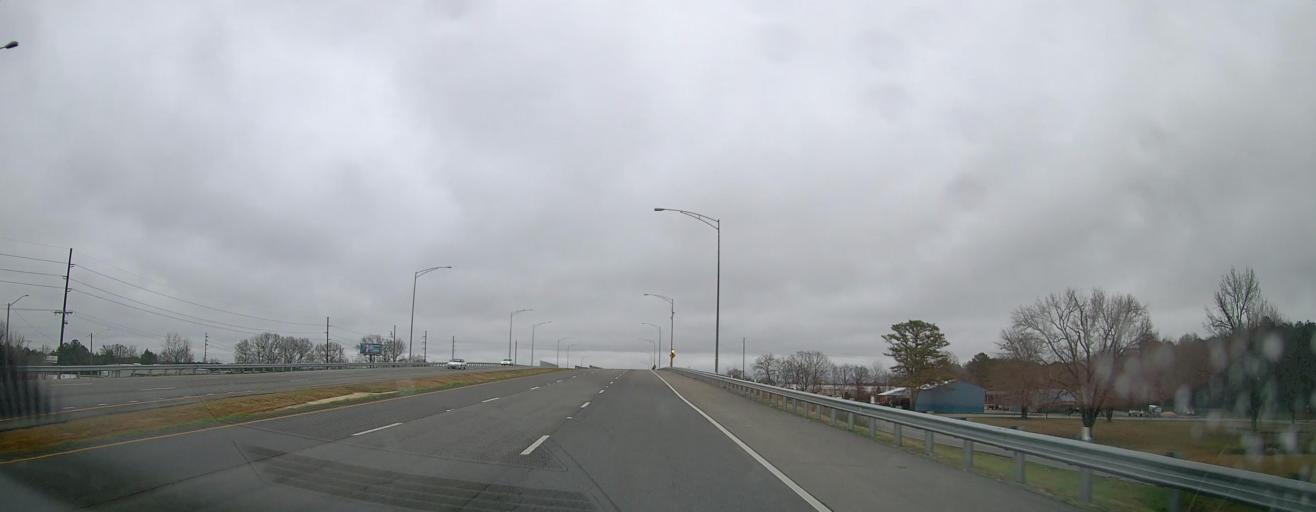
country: US
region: Alabama
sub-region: Morgan County
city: Flint City
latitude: 34.5610
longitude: -86.9840
